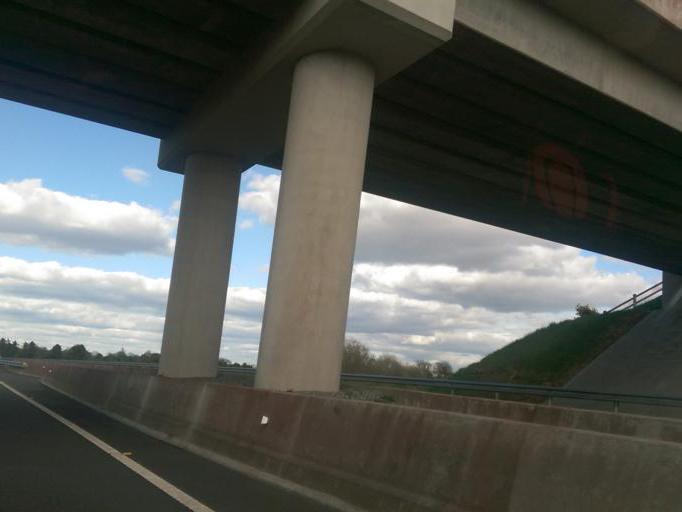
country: IE
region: Leinster
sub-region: An Iarmhi
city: Athlone
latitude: 53.4088
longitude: -8.0190
